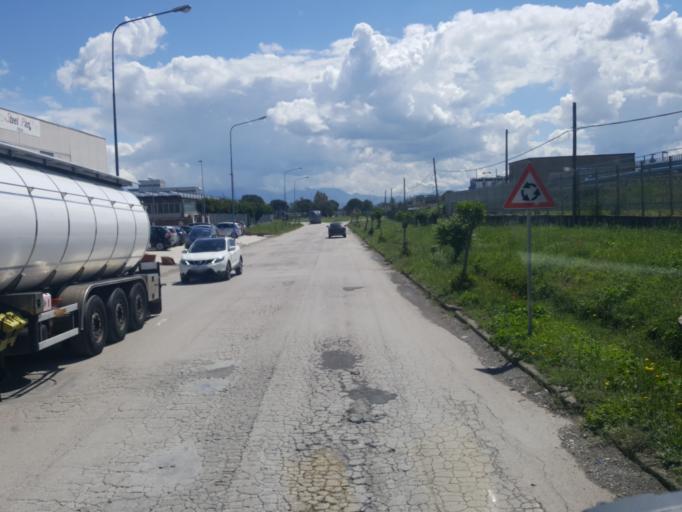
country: IT
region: Campania
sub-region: Provincia di Napoli
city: Pascarola
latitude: 40.9907
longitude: 14.2980
